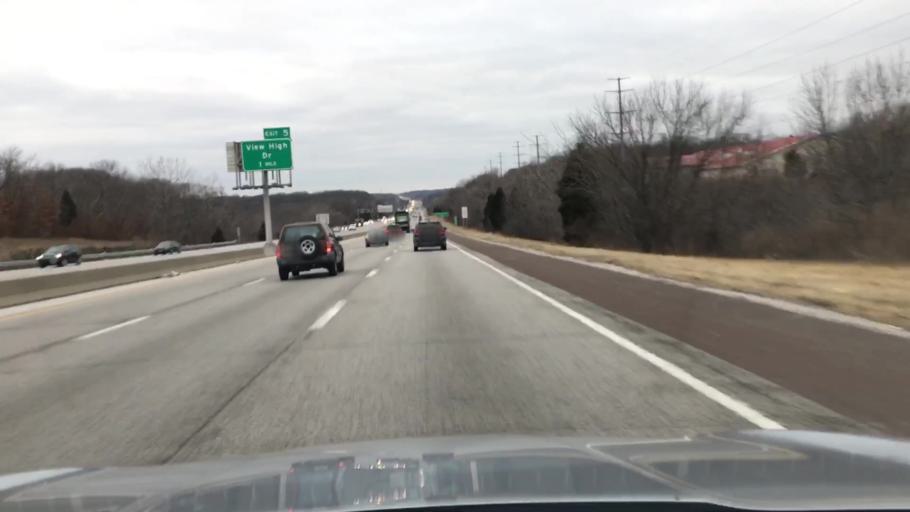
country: US
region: Missouri
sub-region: Jackson County
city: Lees Summit
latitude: 38.9349
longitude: -94.4265
